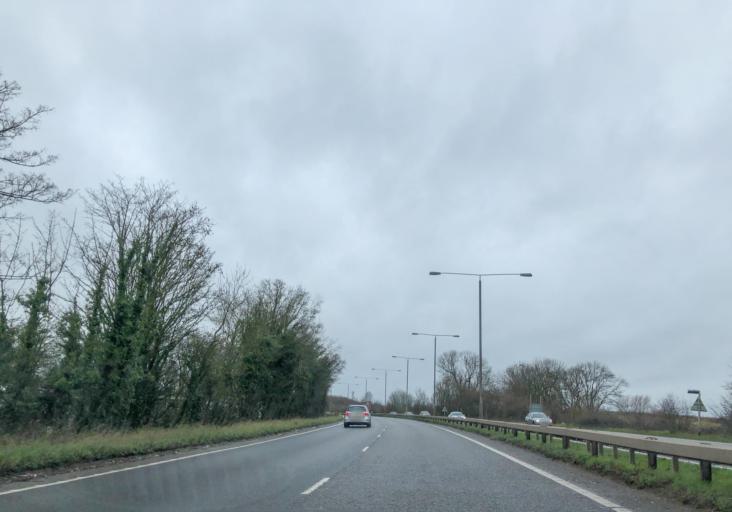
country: GB
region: England
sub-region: Surrey
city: Colnbrook
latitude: 51.4665
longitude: -0.4980
